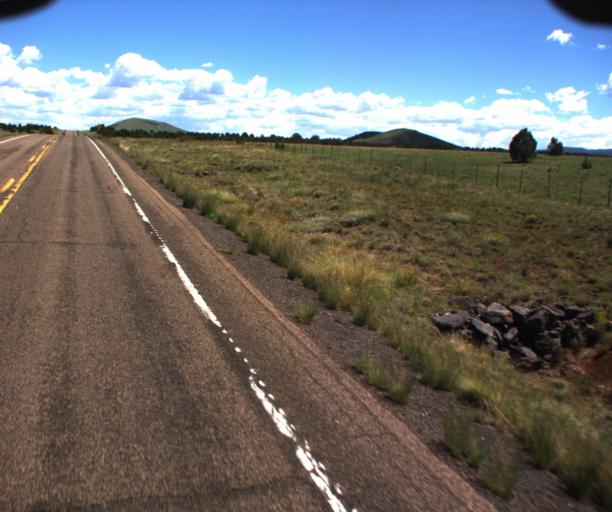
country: US
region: Arizona
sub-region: Apache County
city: Springerville
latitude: 34.2567
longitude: -109.5481
